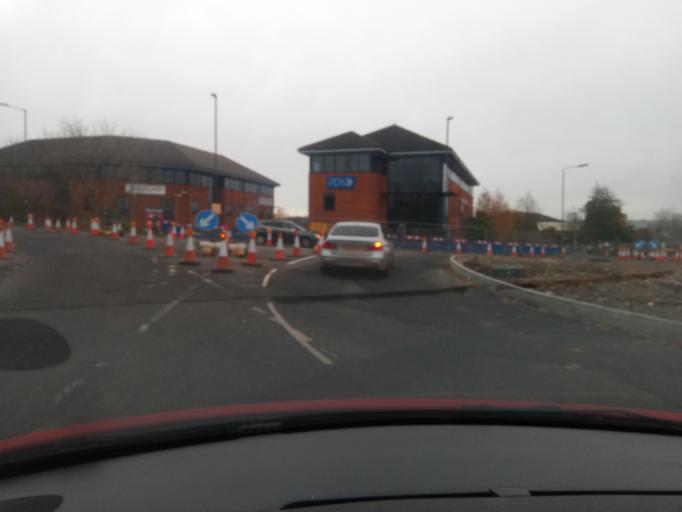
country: GB
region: England
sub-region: Derby
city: Derby
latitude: 52.9152
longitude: -1.4336
